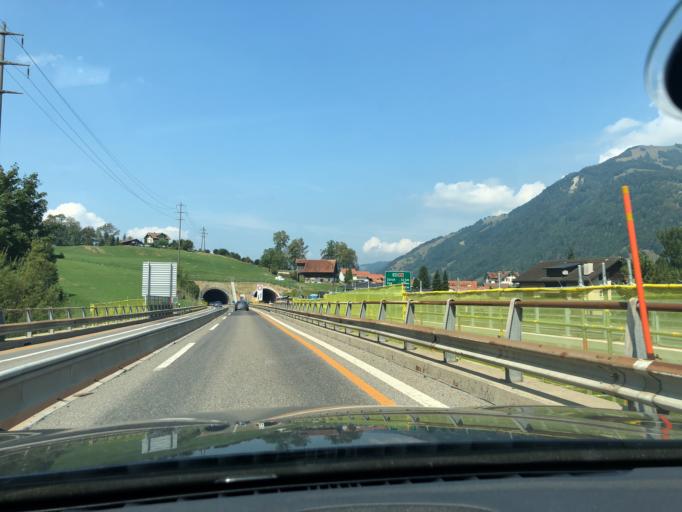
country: CH
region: Schwyz
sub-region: Bezirk Schwyz
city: Goldau
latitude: 47.0460
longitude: 8.5433
